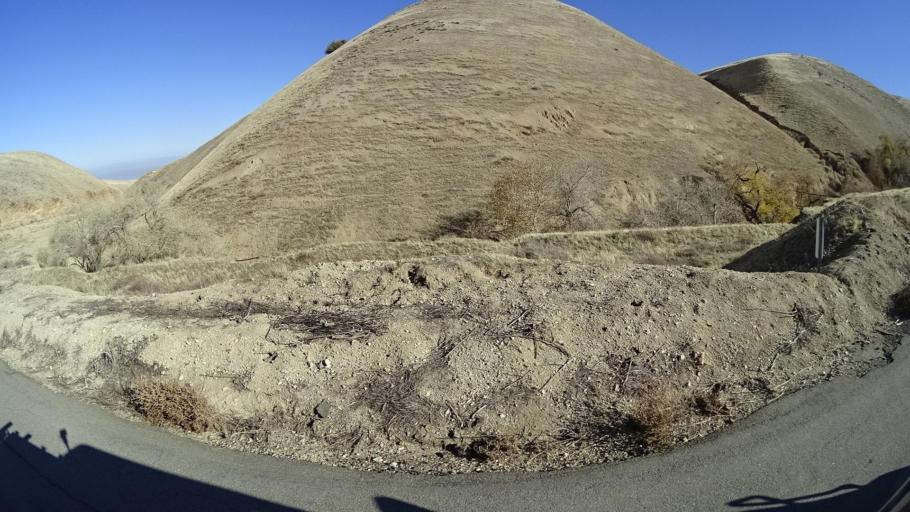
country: US
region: California
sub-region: Kern County
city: Maricopa
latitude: 34.9691
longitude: -119.4147
